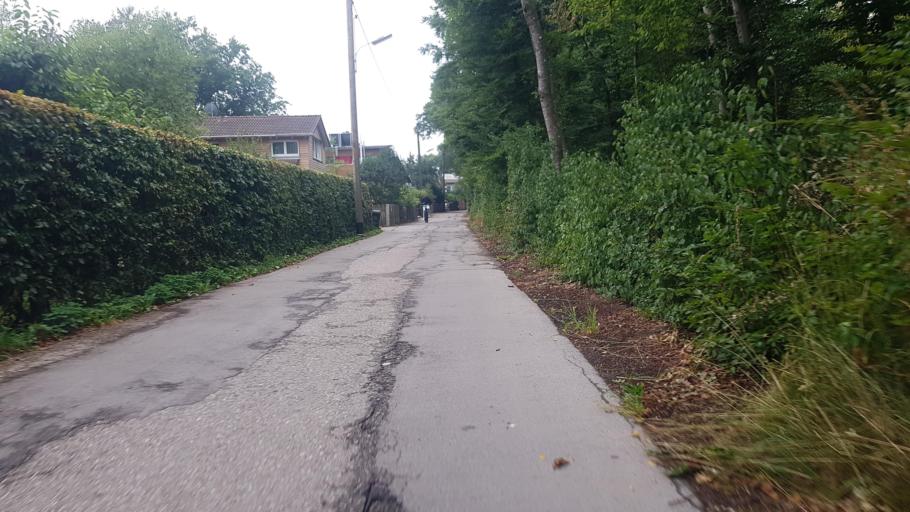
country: DE
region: Bavaria
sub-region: Upper Bavaria
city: Gauting
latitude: 48.0594
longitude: 11.3679
